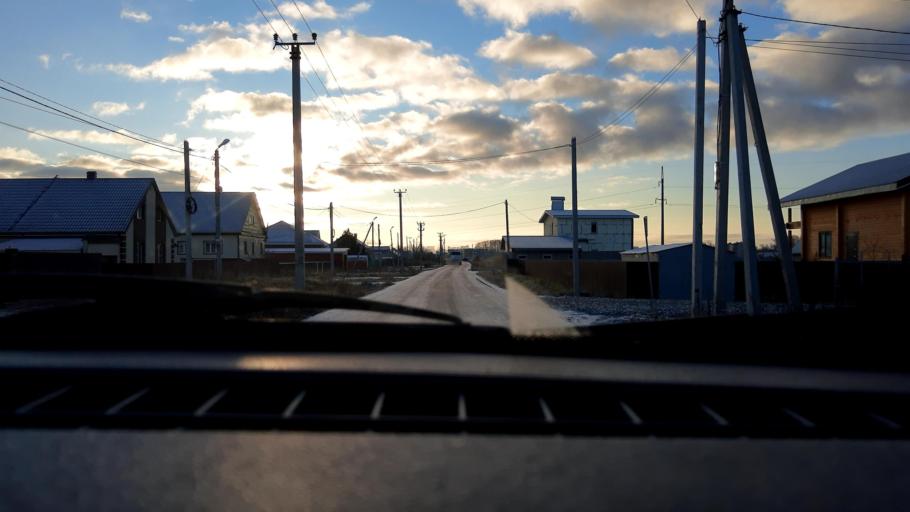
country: RU
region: Bashkortostan
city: Mikhaylovka
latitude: 54.7893
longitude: 55.8254
